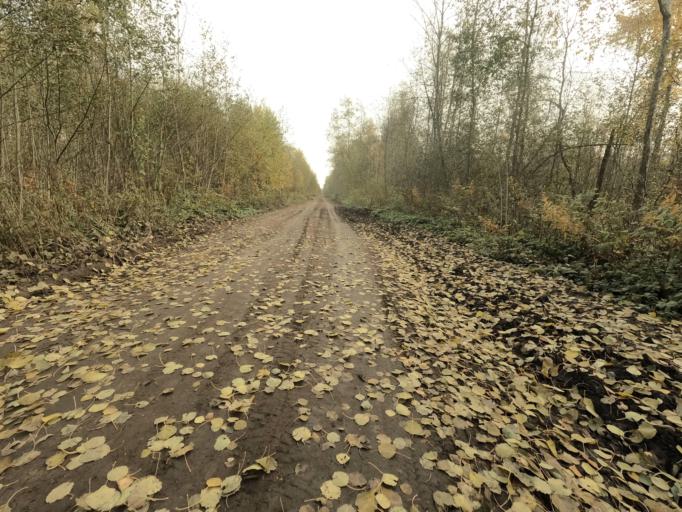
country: RU
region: Novgorod
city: Batetskiy
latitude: 58.8791
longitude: 30.7532
